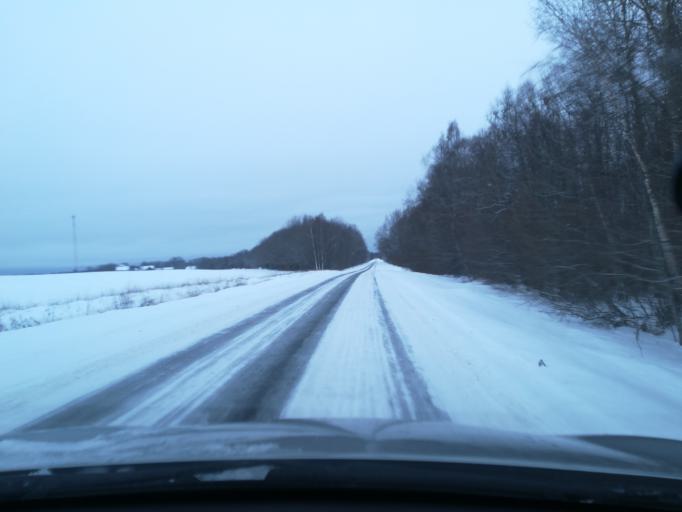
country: EE
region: Harju
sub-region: Keila linn
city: Keila
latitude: 59.3697
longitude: 24.3187
